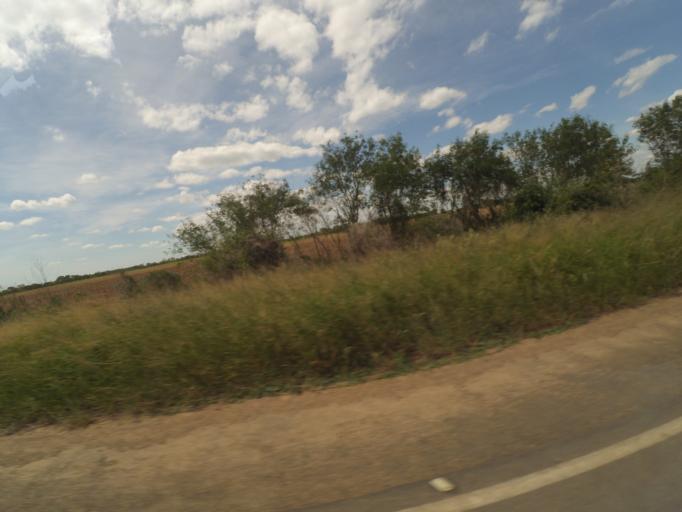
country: BO
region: Santa Cruz
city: Pailon
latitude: -17.5853
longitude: -62.0556
